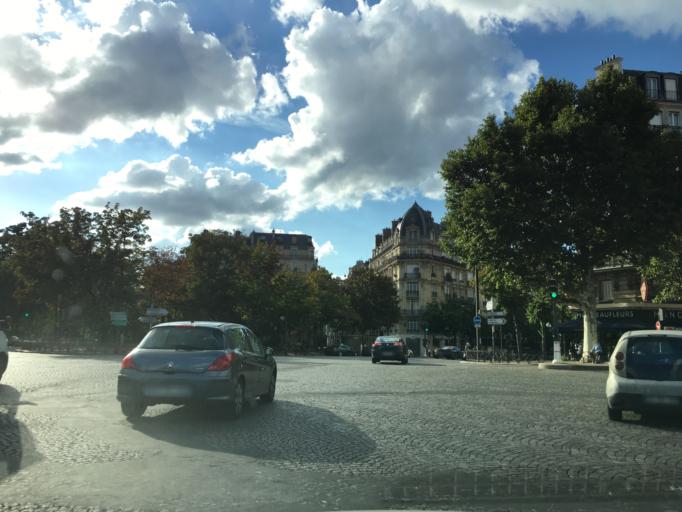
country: FR
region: Ile-de-France
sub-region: Departement du Val-de-Marne
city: Gentilly
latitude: 48.8343
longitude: 2.3329
